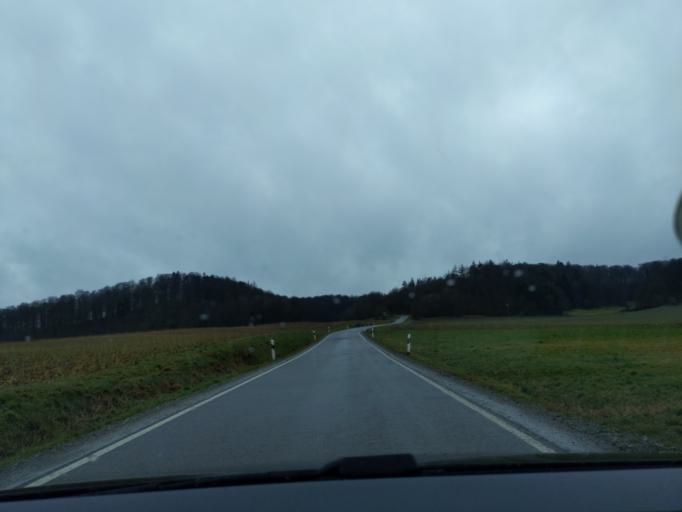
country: DE
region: Hesse
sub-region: Regierungsbezirk Kassel
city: Sachsenhausen
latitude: 51.3006
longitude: 8.9590
